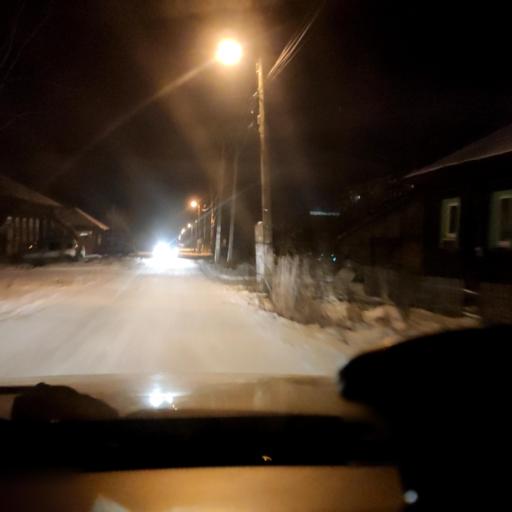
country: RU
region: Perm
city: Perm
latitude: 58.0274
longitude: 56.3222
